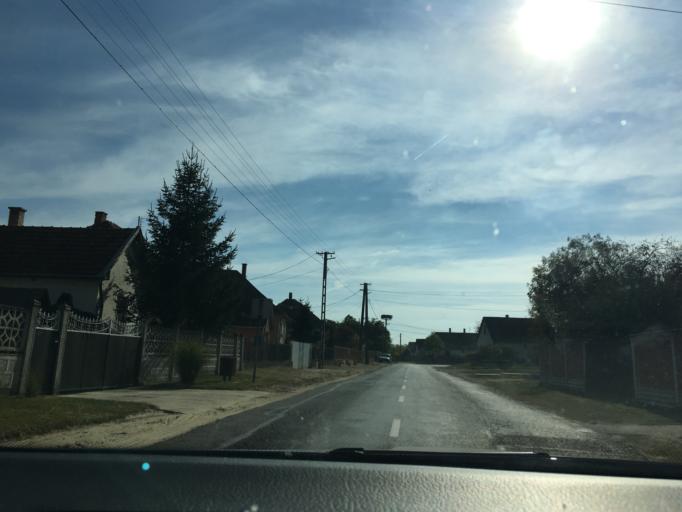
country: HU
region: Hajdu-Bihar
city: Nyirabrany
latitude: 47.5337
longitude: 22.0001
